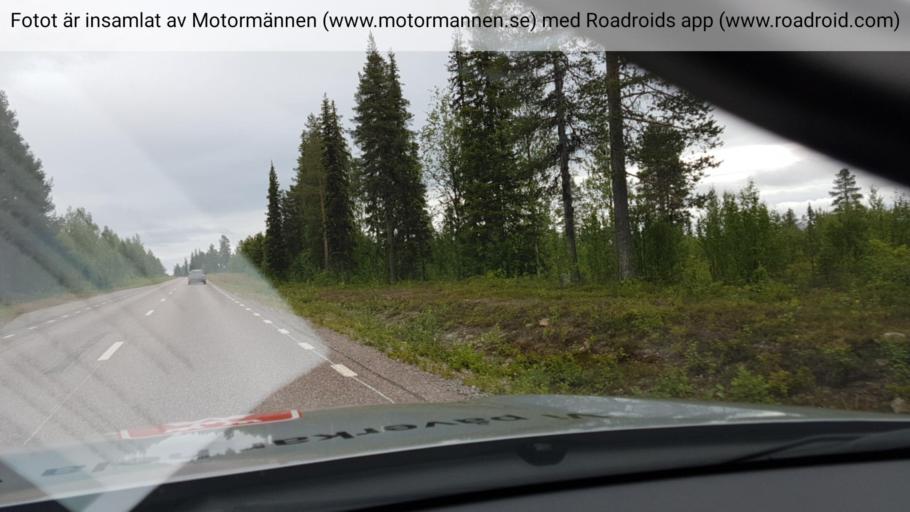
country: SE
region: Norrbotten
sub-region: Gallivare Kommun
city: Gaellivare
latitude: 67.0493
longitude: 21.6086
